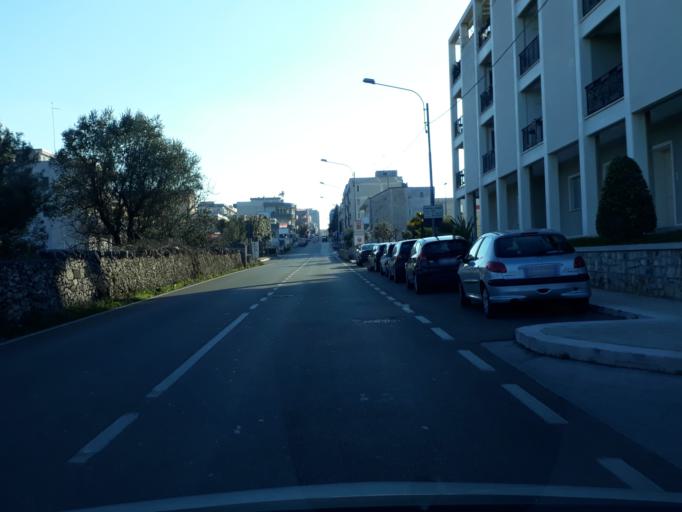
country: IT
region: Apulia
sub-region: Provincia di Bari
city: Locorotondo
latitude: 40.7615
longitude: 17.3300
